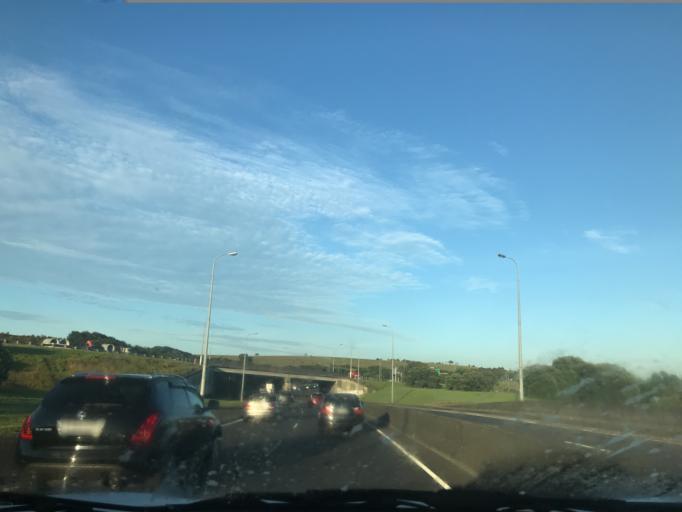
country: NZ
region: Auckland
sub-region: Auckland
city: Tamaki
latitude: -36.9162
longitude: 174.8358
